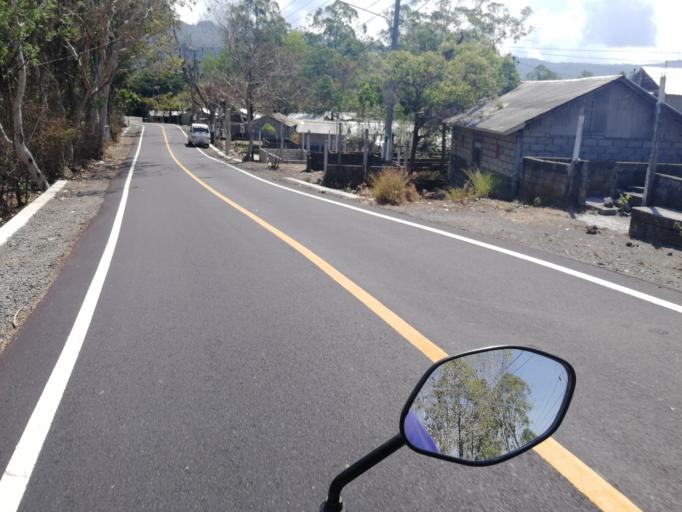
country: ID
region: Bali
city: Banjar Kedisan
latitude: -8.2656
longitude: 115.3858
